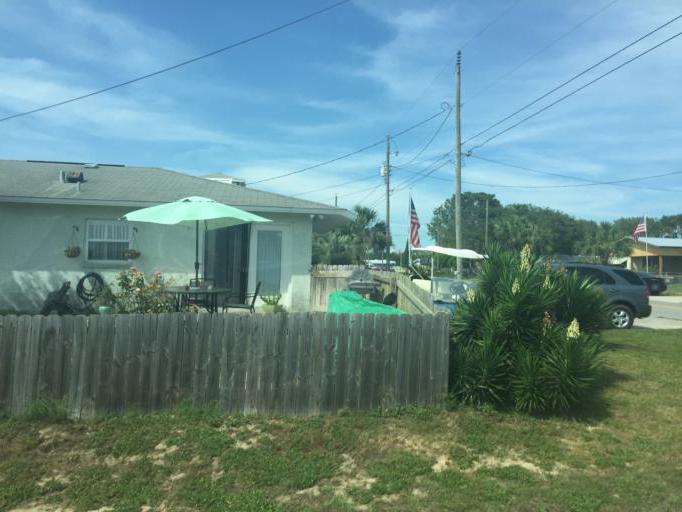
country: US
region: Florida
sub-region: Bay County
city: Laguna Beach
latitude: 30.2490
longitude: -85.9344
